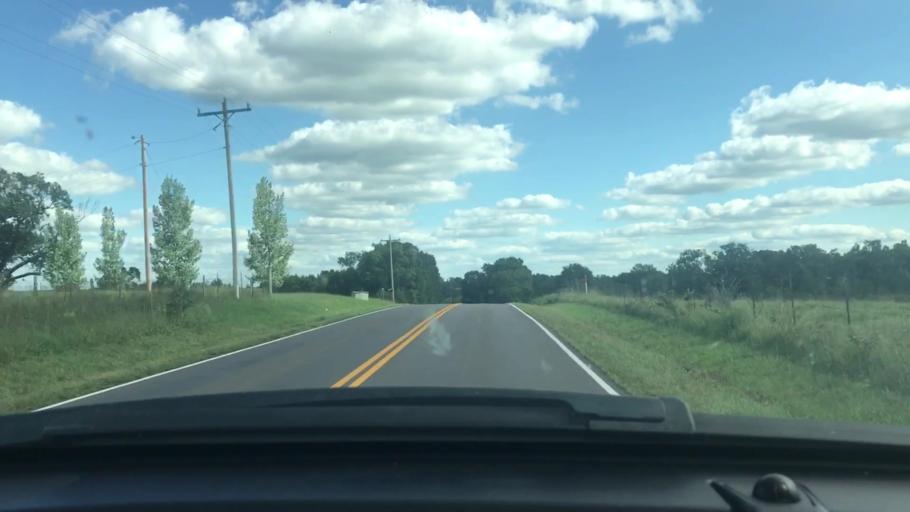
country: US
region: Missouri
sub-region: Wright County
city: Mountain Grove
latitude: 37.3082
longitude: -92.3149
